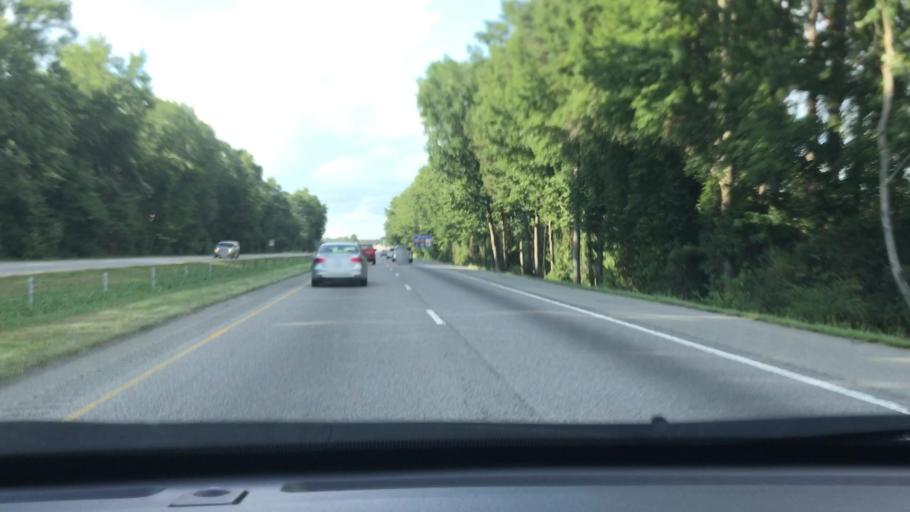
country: US
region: North Carolina
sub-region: Robeson County
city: Saint Pauls
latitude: 34.8002
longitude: -78.9909
